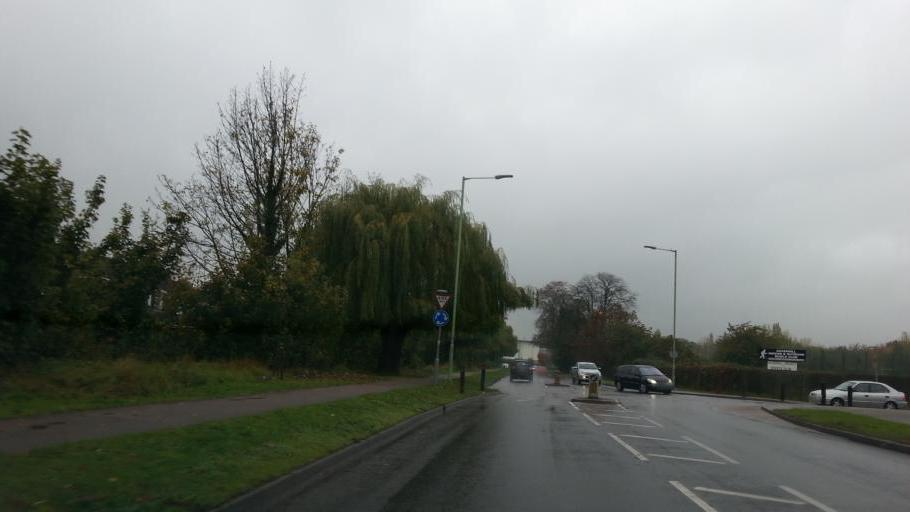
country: GB
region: England
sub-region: Suffolk
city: Haverhill
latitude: 52.0787
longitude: 0.4466
